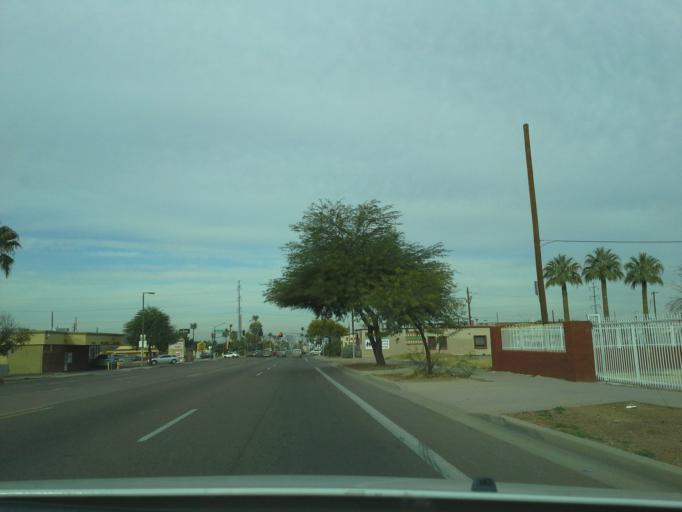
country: US
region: Arizona
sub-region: Maricopa County
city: Phoenix
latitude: 33.3761
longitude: -112.0732
